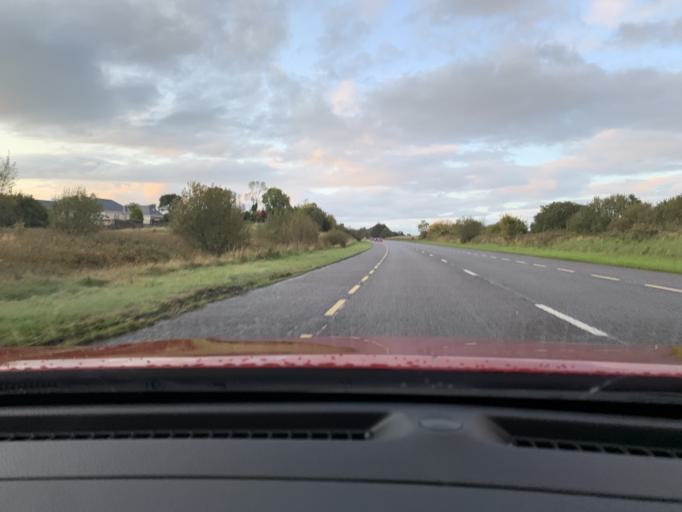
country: IE
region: Connaught
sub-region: Roscommon
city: Boyle
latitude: 54.0505
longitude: -8.3400
